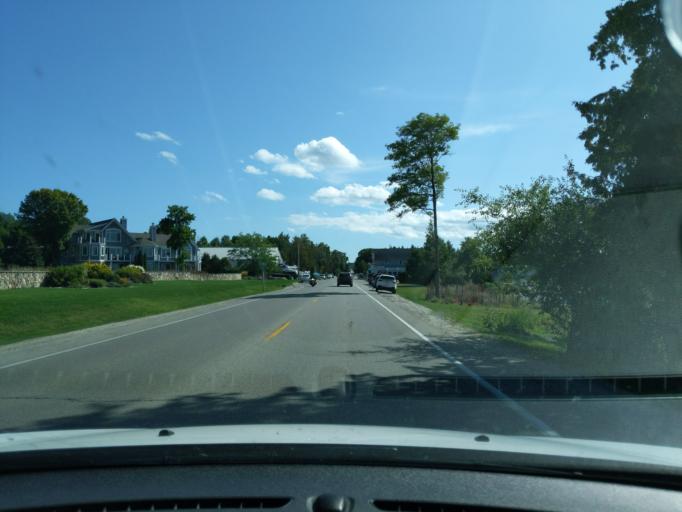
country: US
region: Wisconsin
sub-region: Door County
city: Sturgeon Bay
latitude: 45.2042
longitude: -87.1189
